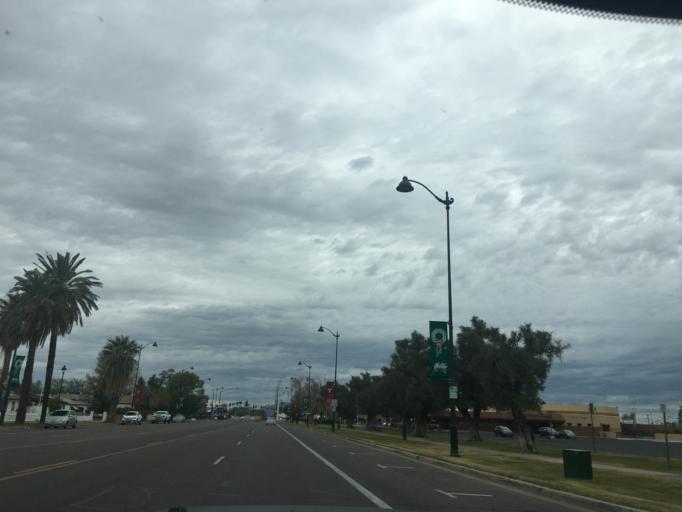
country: US
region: Arizona
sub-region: Maricopa County
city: Mesa
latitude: 33.4199
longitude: -111.8314
